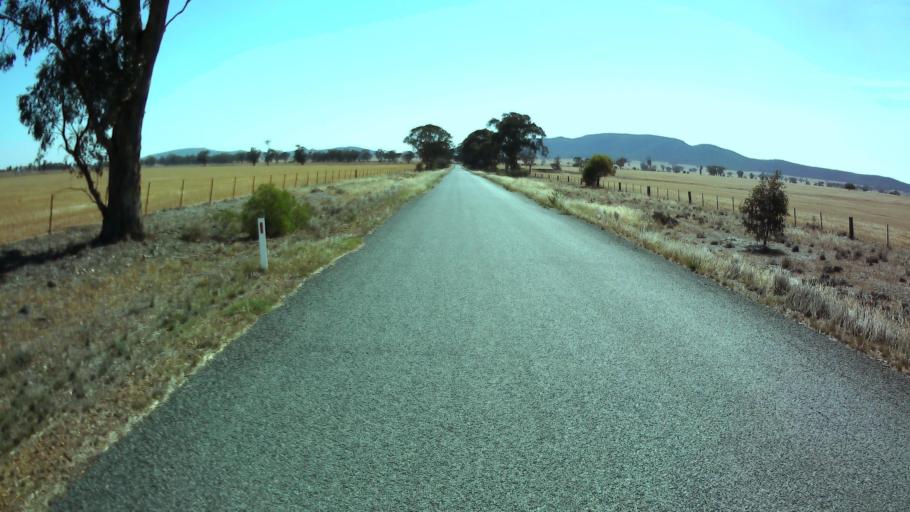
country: AU
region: New South Wales
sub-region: Weddin
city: Grenfell
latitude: -33.7514
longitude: 147.8682
